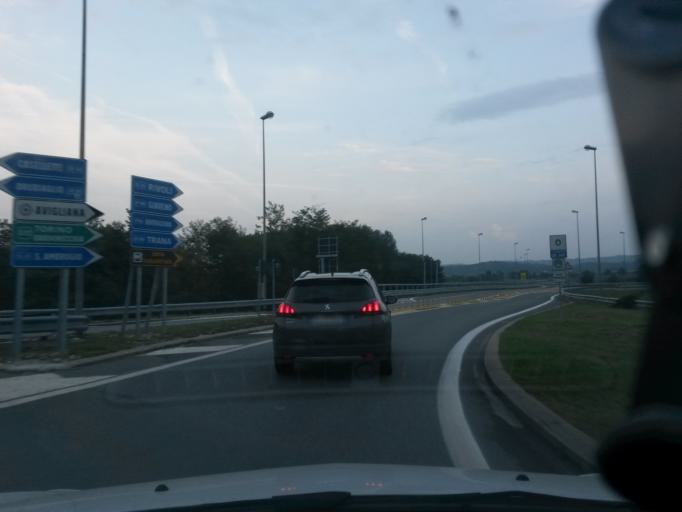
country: IT
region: Piedmont
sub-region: Provincia di Torino
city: Drubiaglio-Grangia
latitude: 45.0945
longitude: 7.4182
